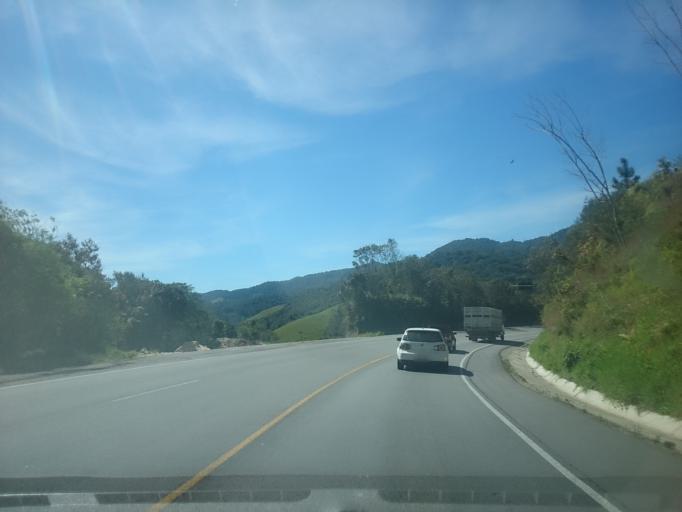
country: BR
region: Santa Catarina
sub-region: Santo Amaro Da Imperatriz
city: Santo Amaro da Imperatriz
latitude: -27.7147
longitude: -48.9402
